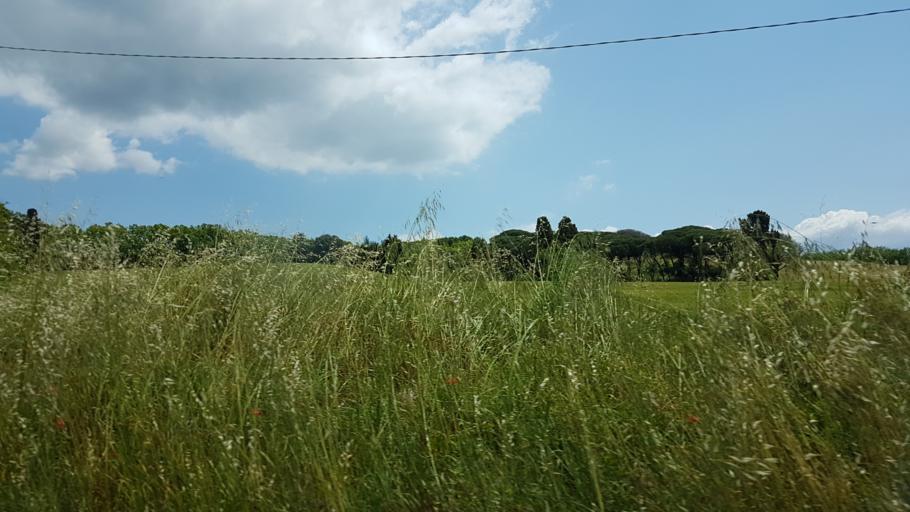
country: IT
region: Tuscany
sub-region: Provincia di Livorno
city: Collesalvetti
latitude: 43.5732
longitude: 10.4759
